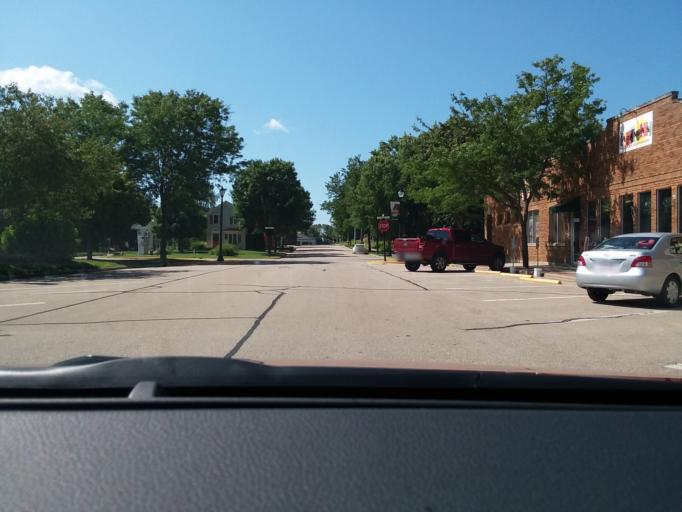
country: US
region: Wisconsin
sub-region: Dane County
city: De Forest
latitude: 43.2468
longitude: -89.3416
